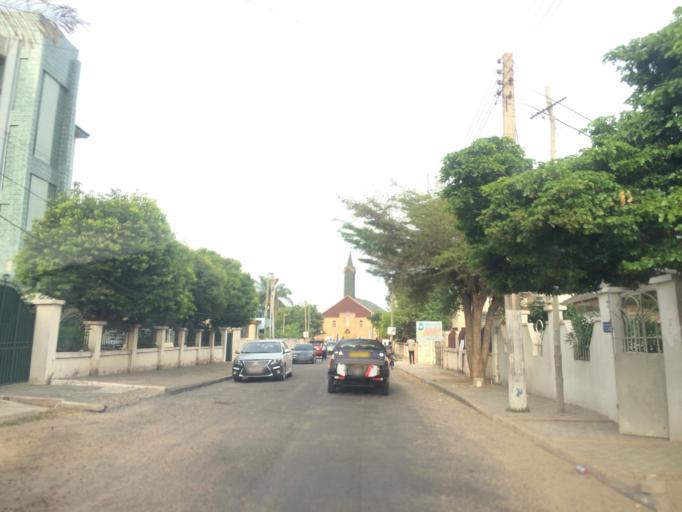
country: GH
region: Greater Accra
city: Accra
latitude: 5.5539
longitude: -0.1860
